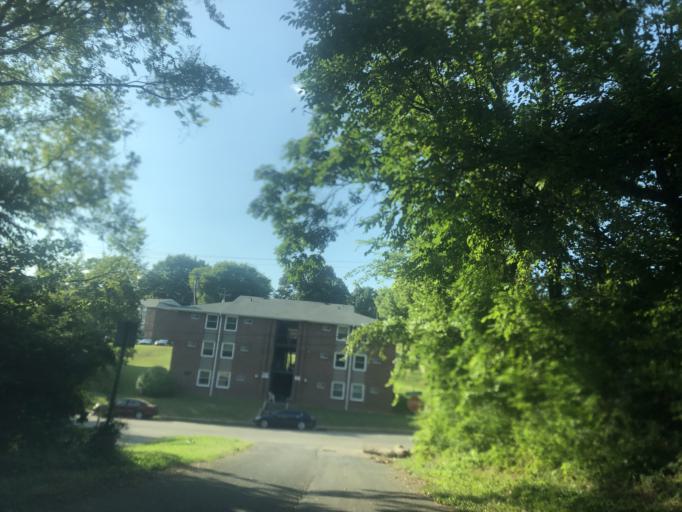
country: US
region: Tennessee
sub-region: Davidson County
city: Nashville
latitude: 36.1637
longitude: -86.7538
